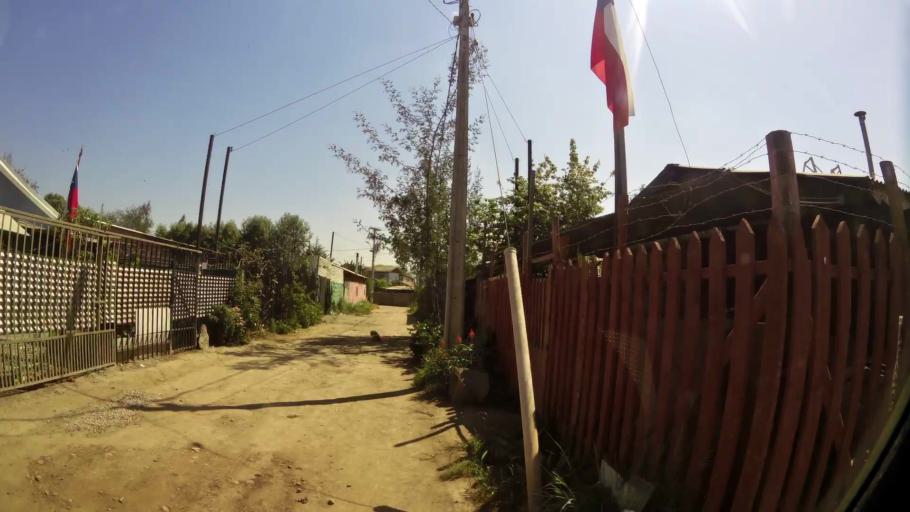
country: CL
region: Santiago Metropolitan
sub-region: Provincia de Talagante
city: Penaflor
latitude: -33.5923
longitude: -70.8140
